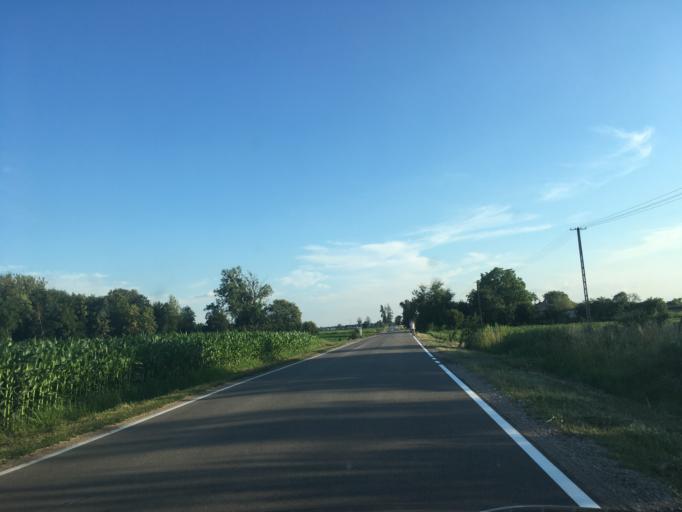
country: PL
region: Masovian Voivodeship
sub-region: Powiat warszawski zachodni
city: Bieniewice
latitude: 52.1387
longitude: 20.5922
